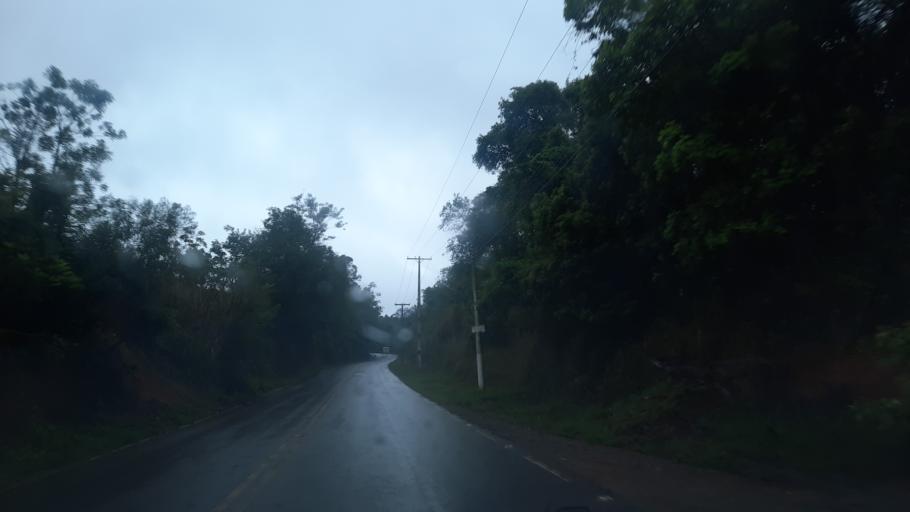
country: BR
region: Sao Paulo
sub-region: Atibaia
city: Atibaia
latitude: -23.0786
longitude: -46.5240
